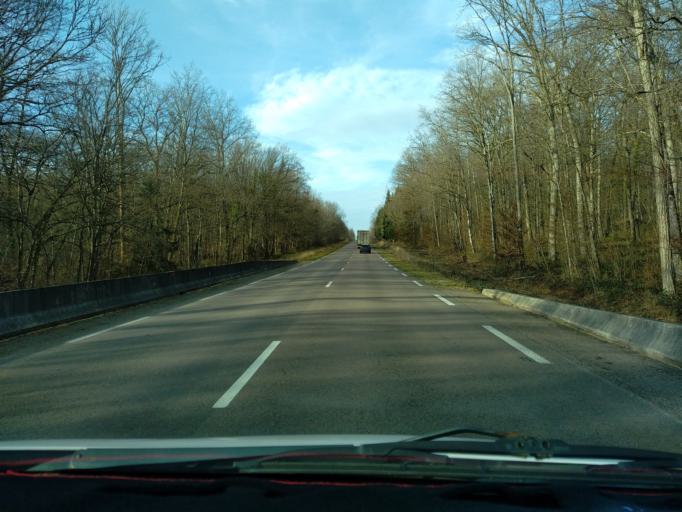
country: FR
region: Franche-Comte
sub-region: Departement de la Haute-Saone
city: Gray
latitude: 47.4054
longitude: 5.6377
